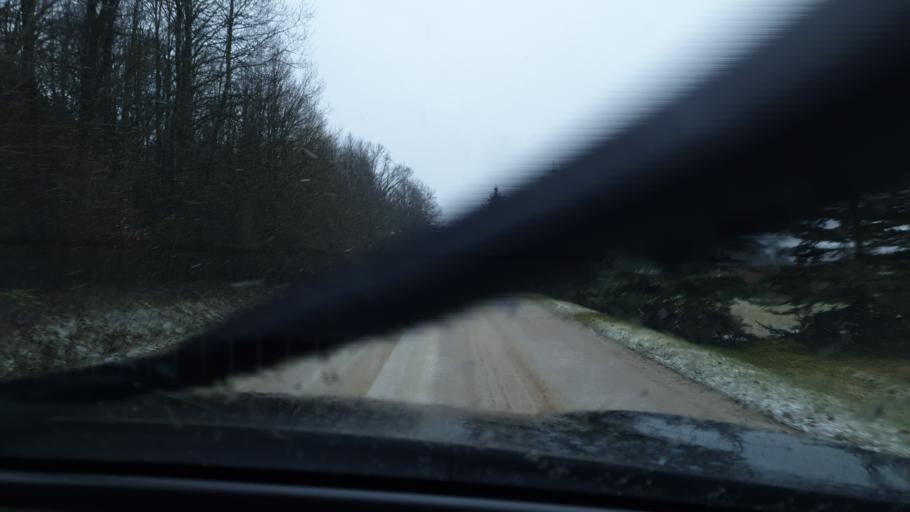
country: LT
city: Jieznas
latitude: 54.5674
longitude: 24.3185
